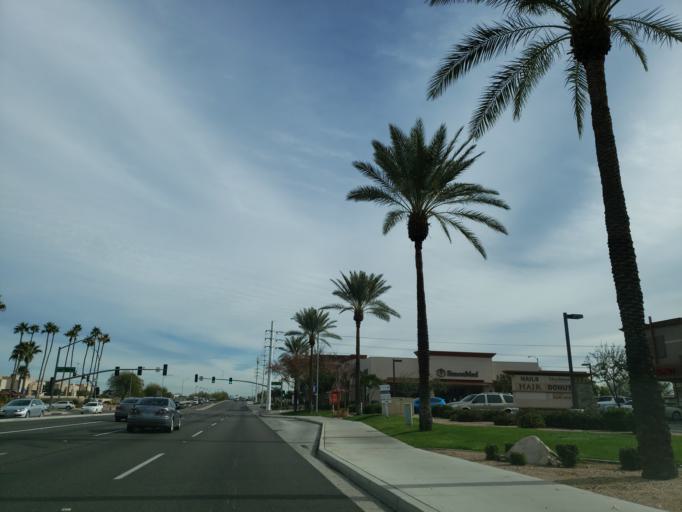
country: US
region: Arizona
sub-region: Maricopa County
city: Sun City
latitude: 33.6096
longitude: -112.2561
